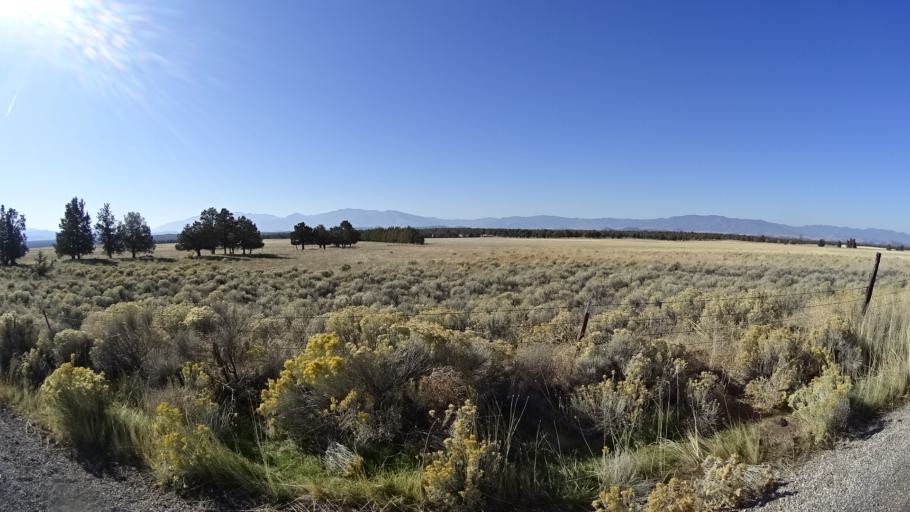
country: US
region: California
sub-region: Siskiyou County
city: Weed
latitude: 41.6171
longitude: -122.3193
